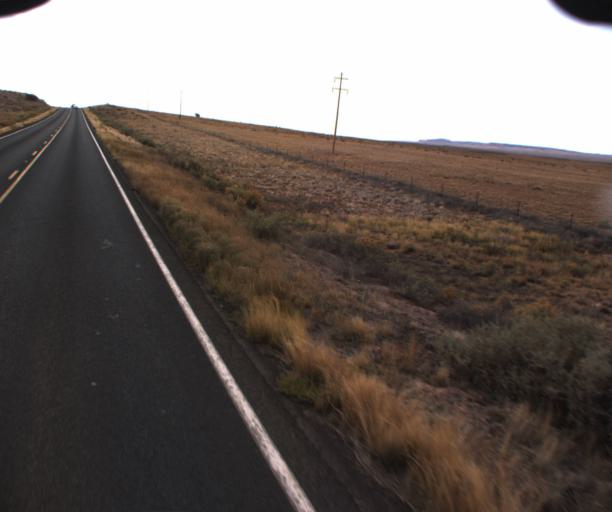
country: US
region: Arizona
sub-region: Apache County
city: Ganado
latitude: 35.8856
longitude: -109.6053
